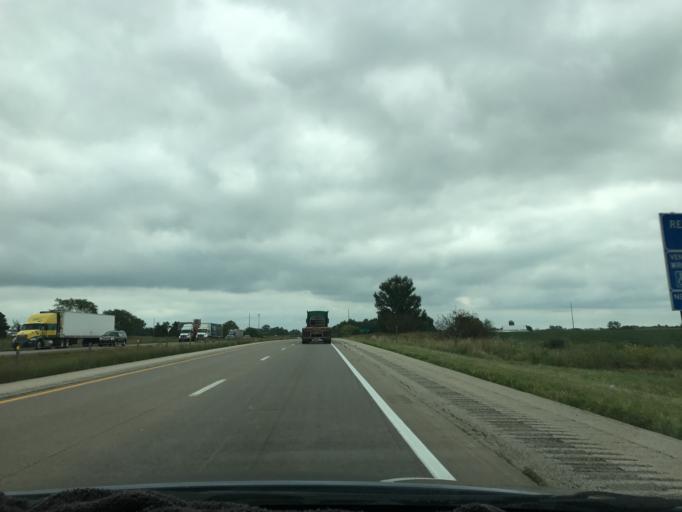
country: US
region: Iowa
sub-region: Scott County
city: Bettendorf
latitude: 41.5962
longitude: -90.5139
